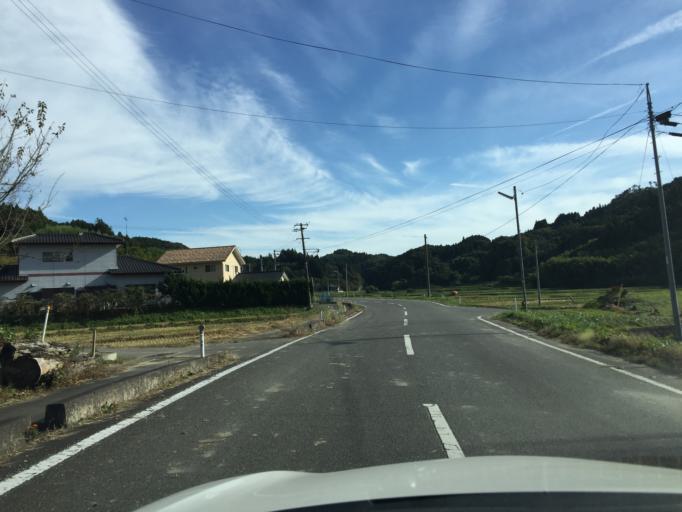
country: JP
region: Fukushima
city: Miharu
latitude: 37.3354
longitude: 140.4878
